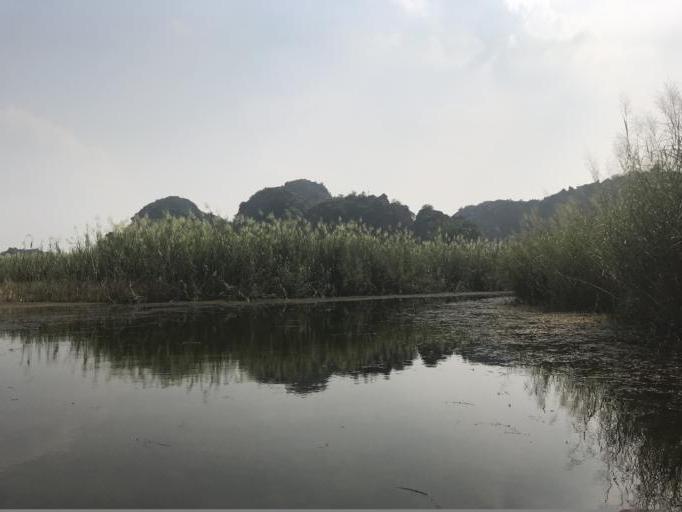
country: VN
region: Ninh Binh
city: Thi Tran Me
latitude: 20.3669
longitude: 105.8907
